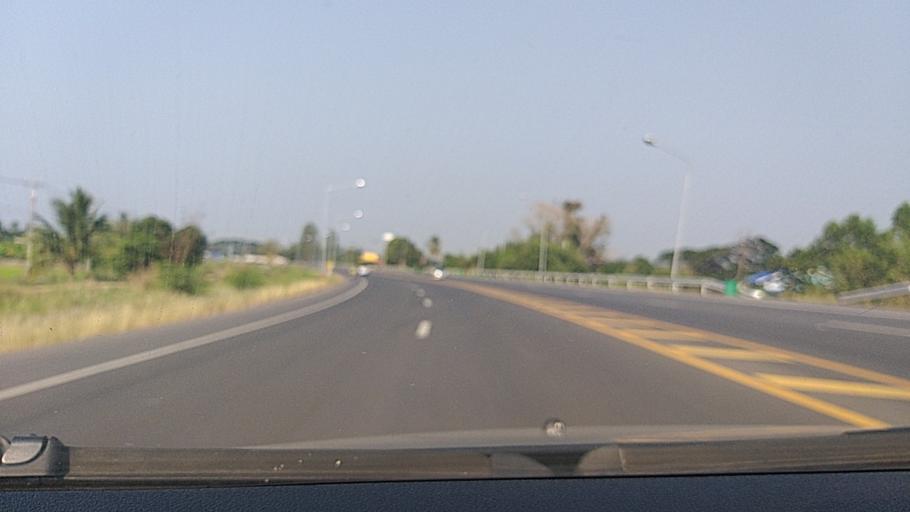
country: TH
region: Sing Buri
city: Phrom Buri
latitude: 14.7897
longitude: 100.4427
